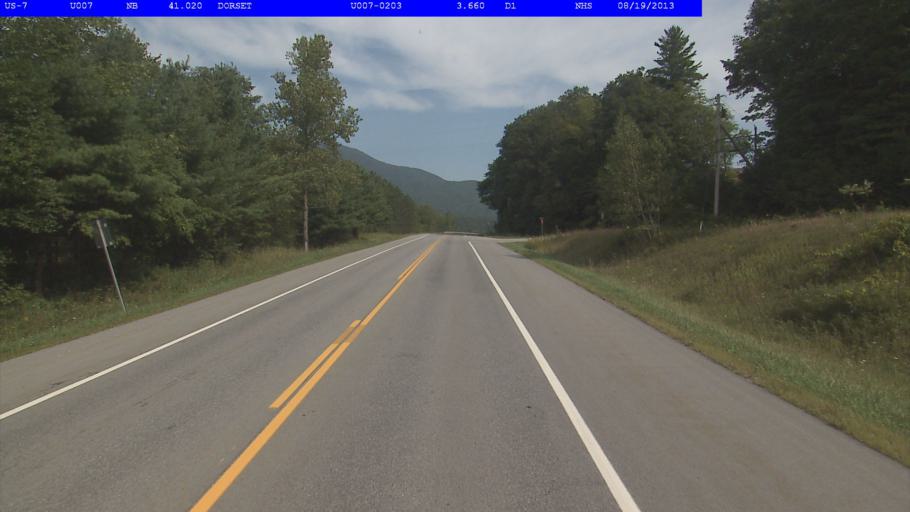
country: US
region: Vermont
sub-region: Bennington County
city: Manchester Center
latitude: 43.2620
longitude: -73.0079
